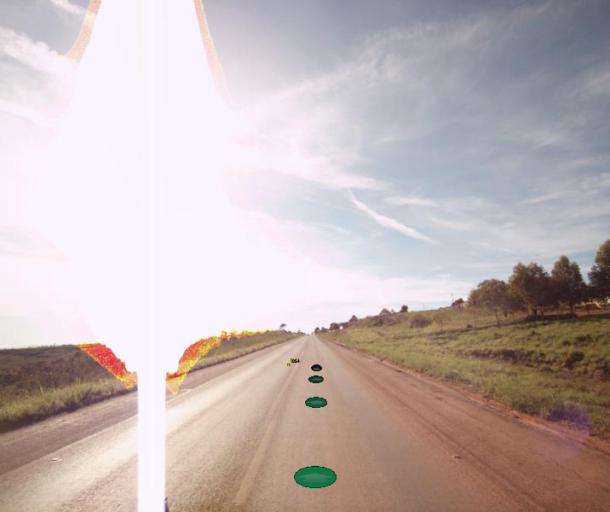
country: BR
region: Federal District
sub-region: Brasilia
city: Brasilia
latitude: -15.7374
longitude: -48.3965
